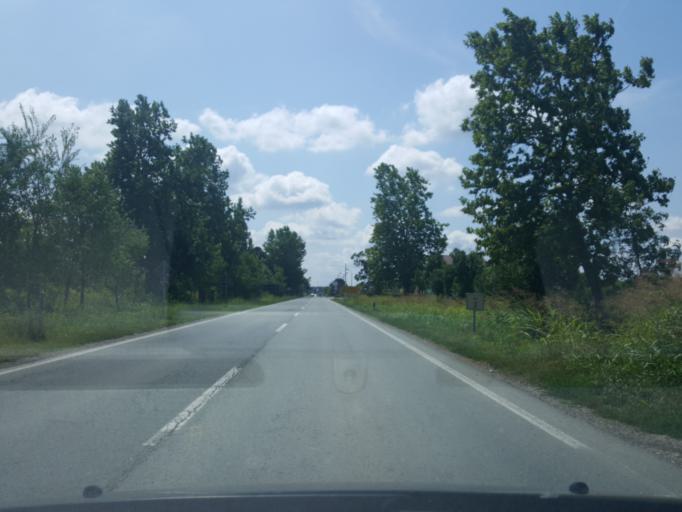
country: RS
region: Autonomna Pokrajina Vojvodina
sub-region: Sremski Okrug
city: Sremska Mitrovica
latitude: 44.9775
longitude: 19.6383
